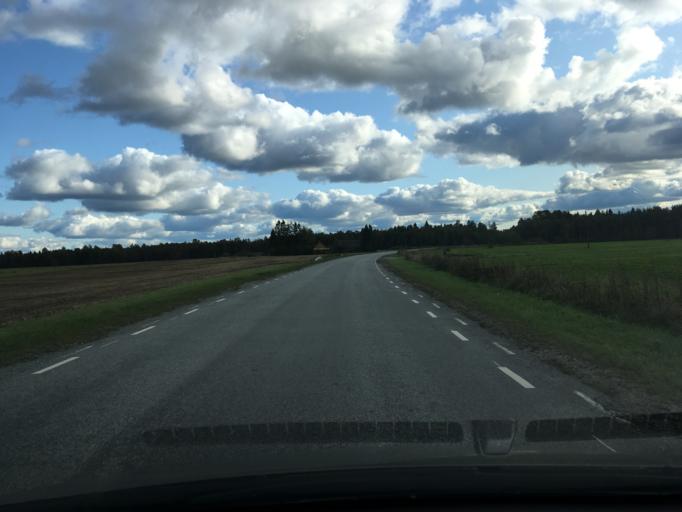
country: EE
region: Harju
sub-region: Raasiku vald
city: Raasiku
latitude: 59.3278
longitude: 25.1596
